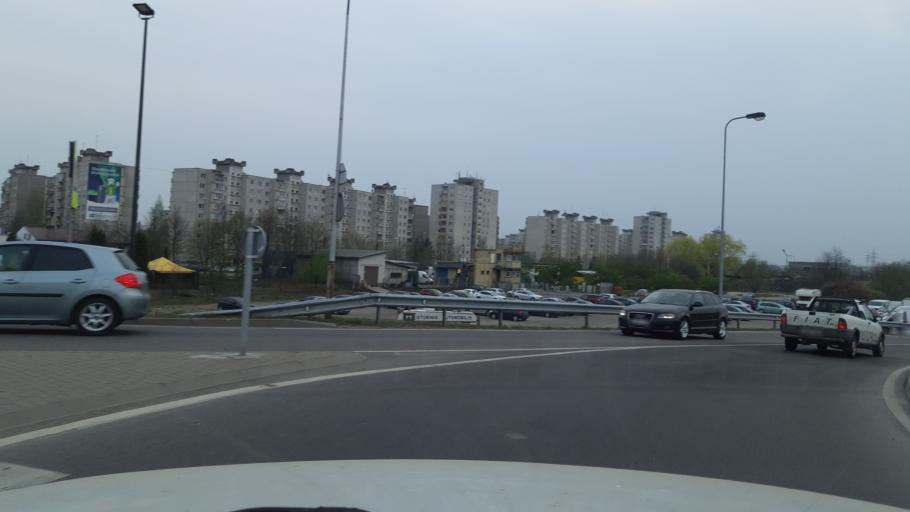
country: LT
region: Kauno apskritis
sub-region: Kaunas
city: Silainiai
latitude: 54.9369
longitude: 23.8984
